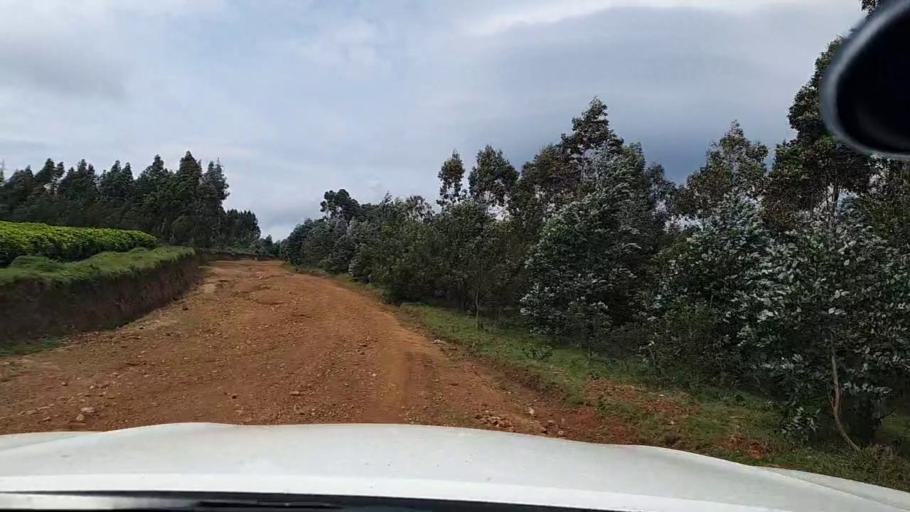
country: RW
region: Western Province
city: Kibuye
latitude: -2.1340
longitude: 29.3772
